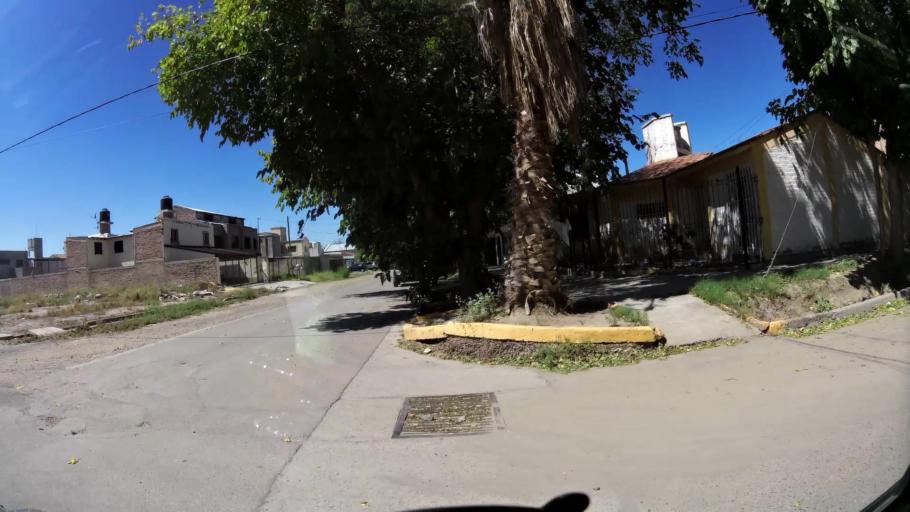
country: AR
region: Mendoza
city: Las Heras
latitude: -32.8498
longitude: -68.8519
